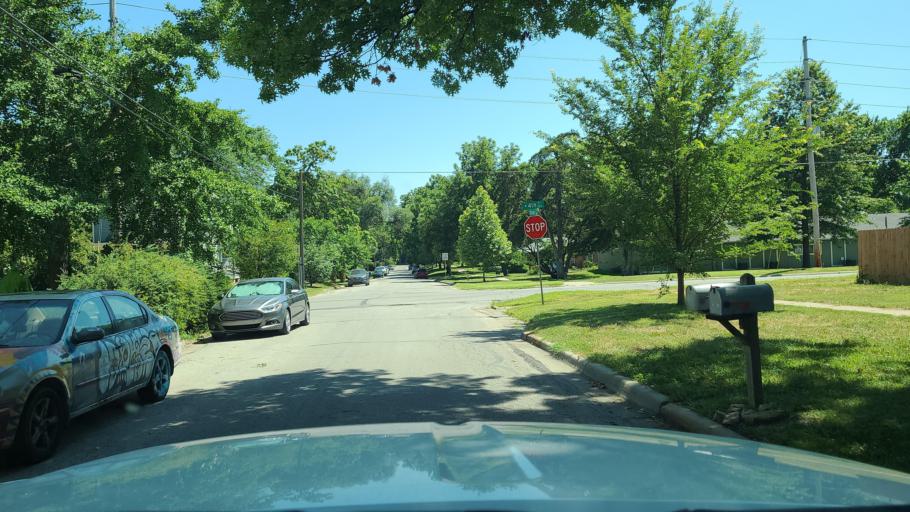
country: US
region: Kansas
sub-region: Douglas County
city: Lawrence
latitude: 38.9773
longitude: -95.2452
